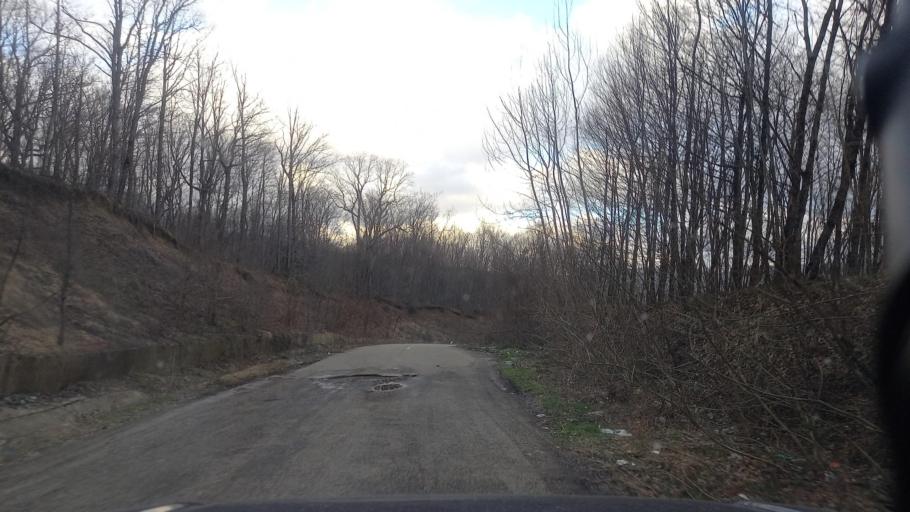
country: RU
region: Krasnodarskiy
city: Lermontovo
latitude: 44.4708
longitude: 38.8231
